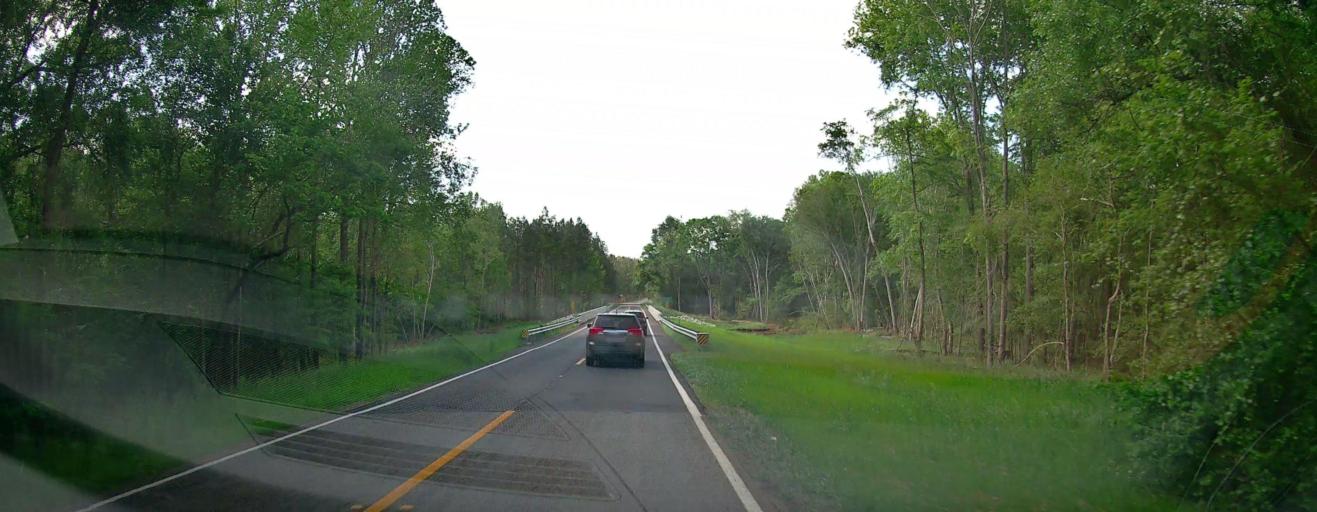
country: US
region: Georgia
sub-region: Laurens County
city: East Dublin
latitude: 32.6989
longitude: -82.9123
